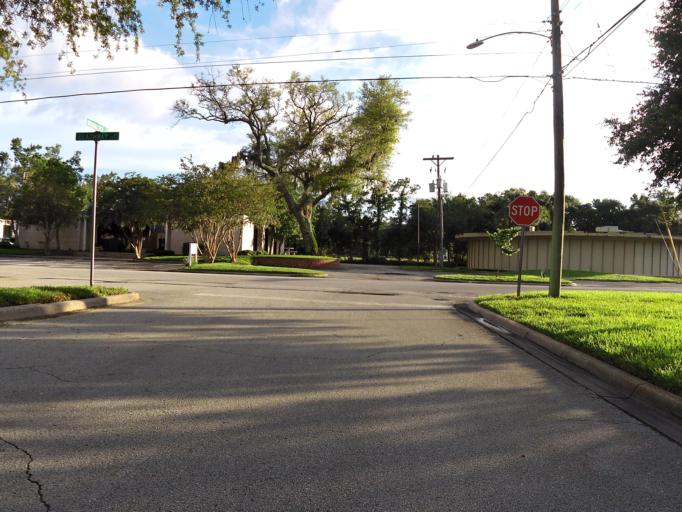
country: US
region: Florida
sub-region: Duval County
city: Jacksonville
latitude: 30.3014
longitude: -81.6208
